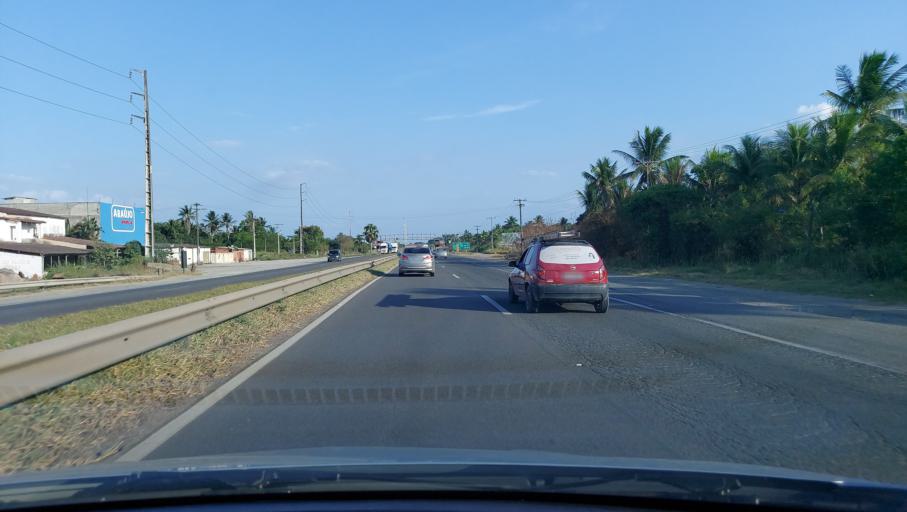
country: BR
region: Bahia
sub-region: Conceicao Do Jacuipe
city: Conceicao do Jacuipe
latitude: -12.3812
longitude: -38.7979
